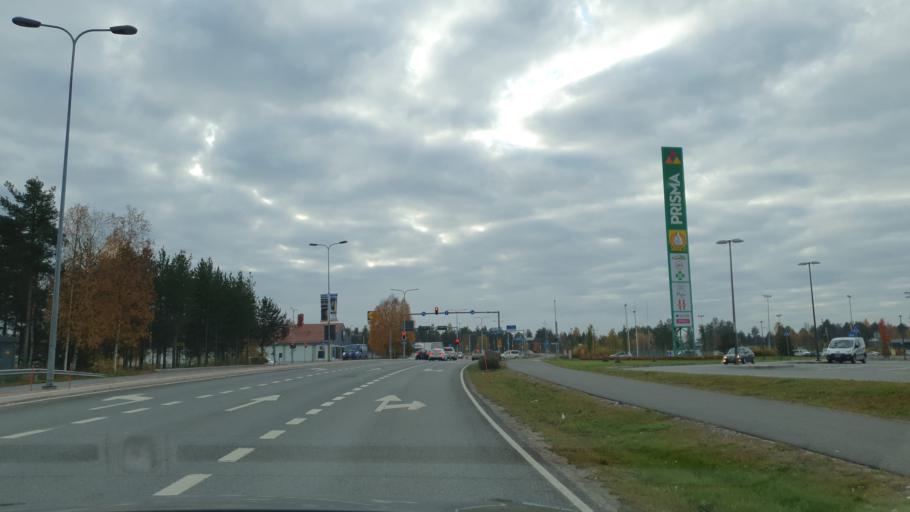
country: FI
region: Lapland
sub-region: Rovaniemi
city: Rovaniemi
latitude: 66.4927
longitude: 25.6918
